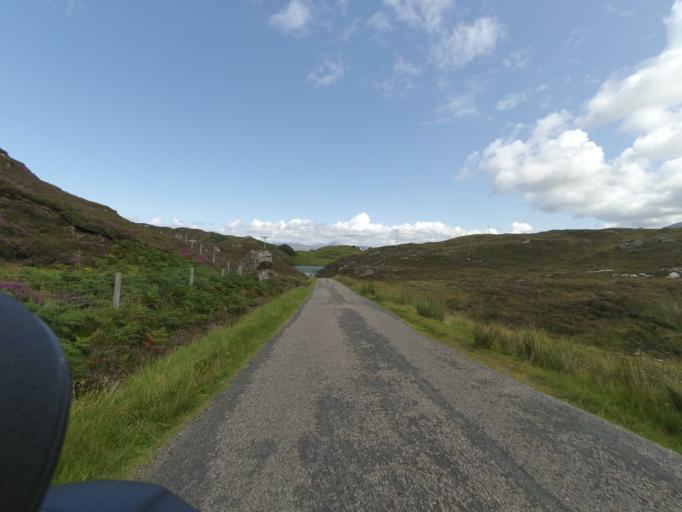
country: GB
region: Scotland
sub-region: Highland
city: Ullapool
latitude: 58.2417
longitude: -5.1941
